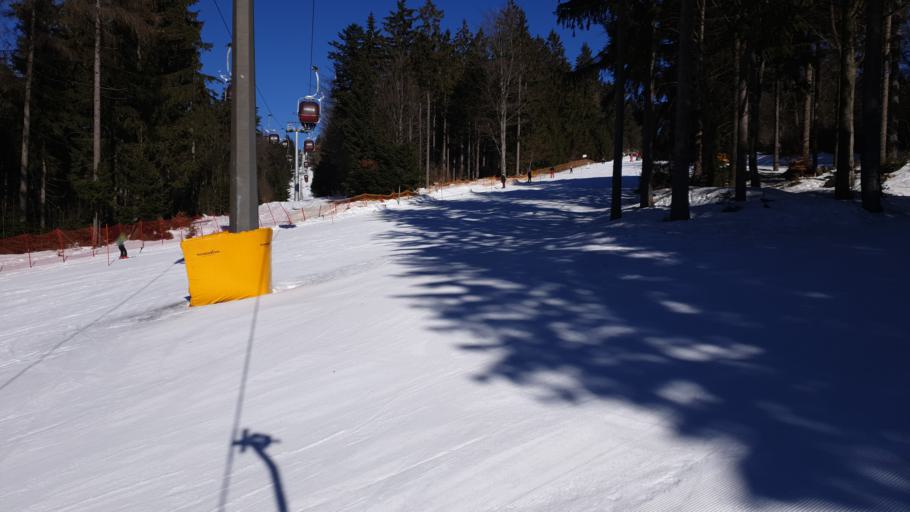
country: DE
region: Bavaria
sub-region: Upper Franconia
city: Warmensteinach
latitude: 50.0144
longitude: 11.8087
